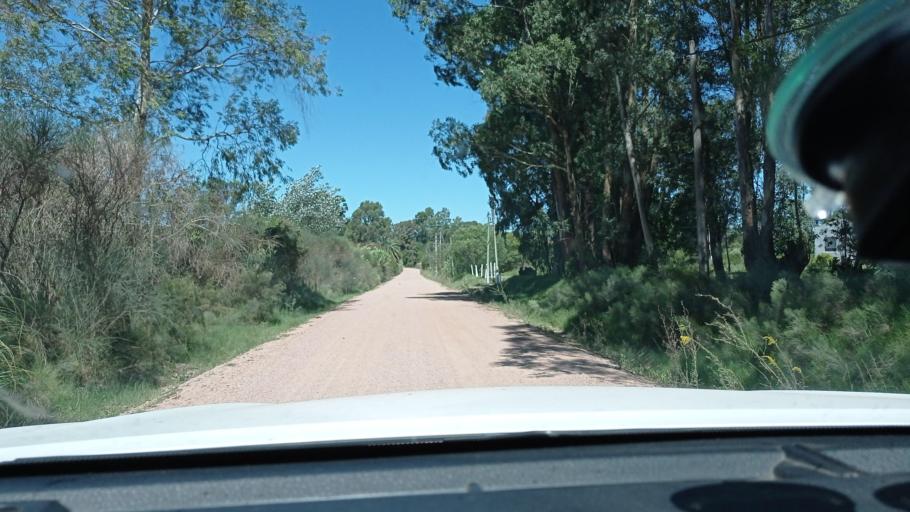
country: UY
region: Canelones
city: La Paz
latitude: -34.7591
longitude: -56.1808
